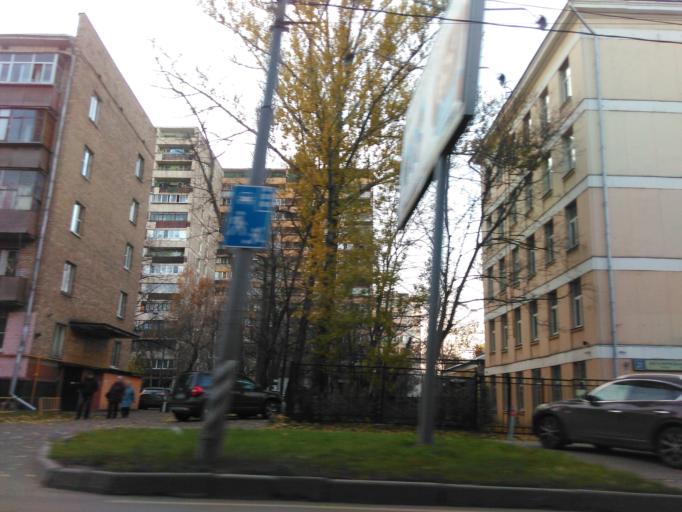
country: RU
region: Moscow
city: Ostankinskiy
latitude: 55.8285
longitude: 37.6014
